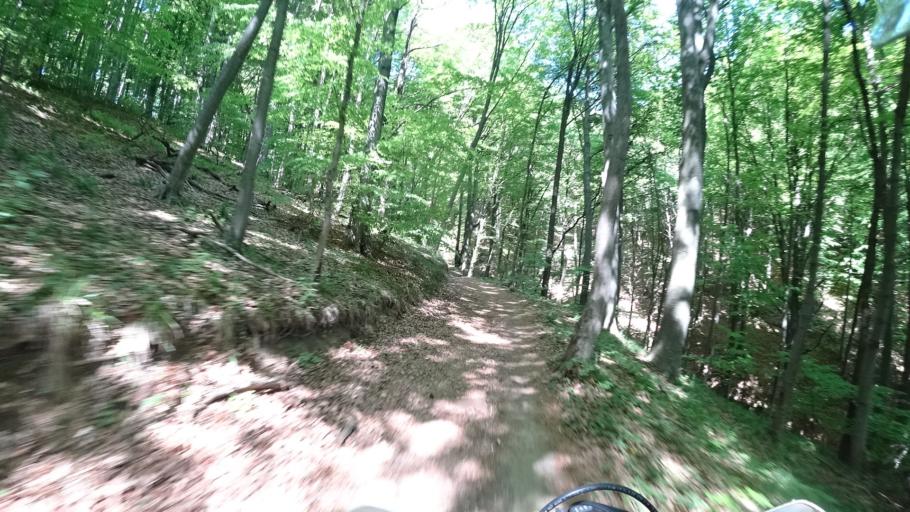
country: HR
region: Zagrebacka
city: Jablanovec
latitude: 45.8752
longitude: 15.8921
